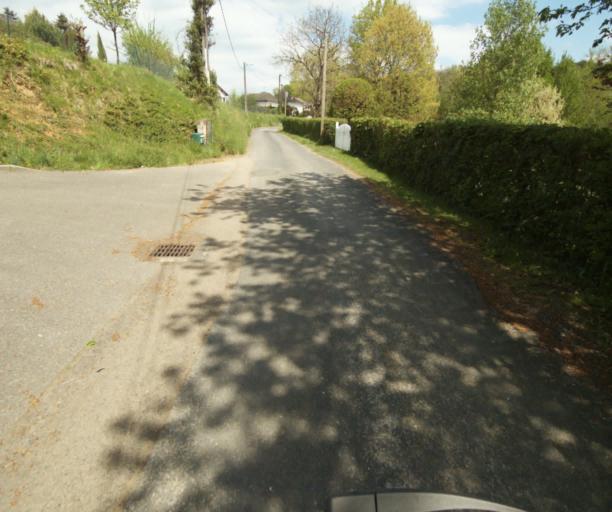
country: FR
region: Limousin
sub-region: Departement de la Correze
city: Tulle
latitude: 45.2826
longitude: 1.7753
